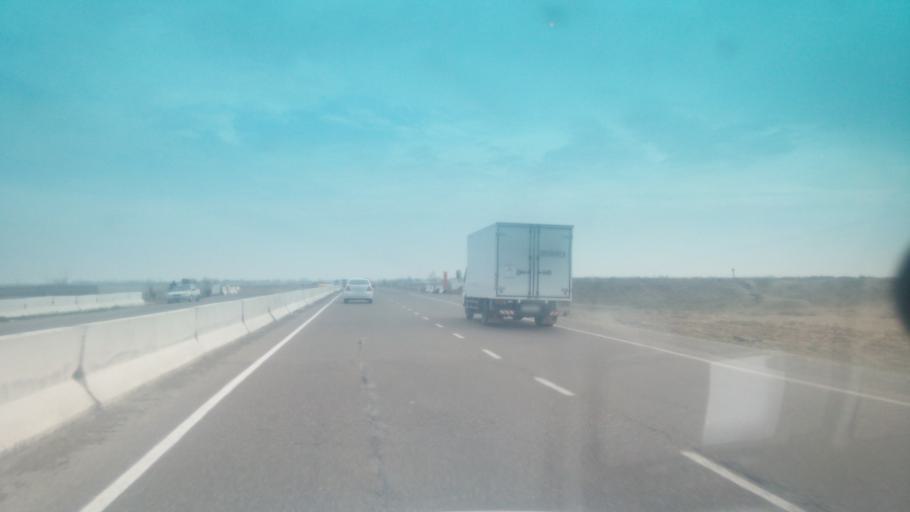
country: KZ
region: Ongtustik Qazaqstan
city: Myrzakent
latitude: 40.5123
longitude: 68.4929
